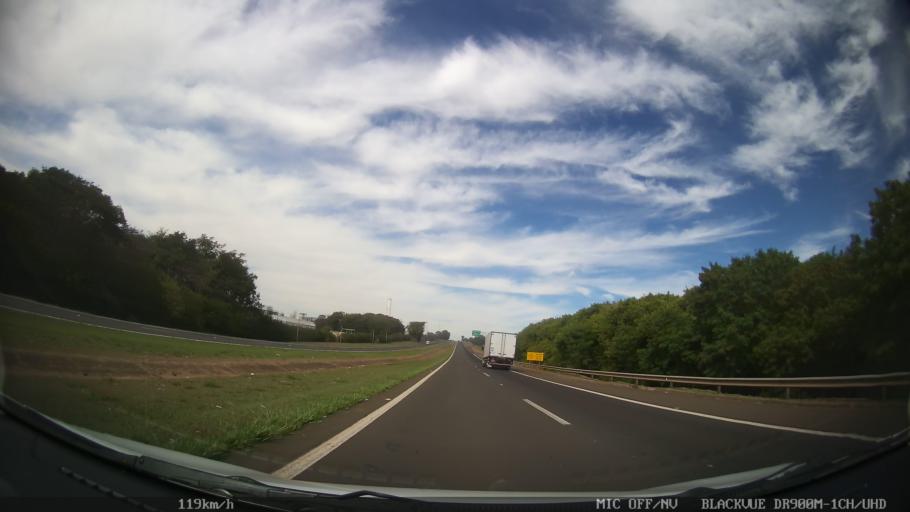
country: BR
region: Sao Paulo
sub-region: Matao
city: Matao
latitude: -21.5872
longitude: -48.4459
